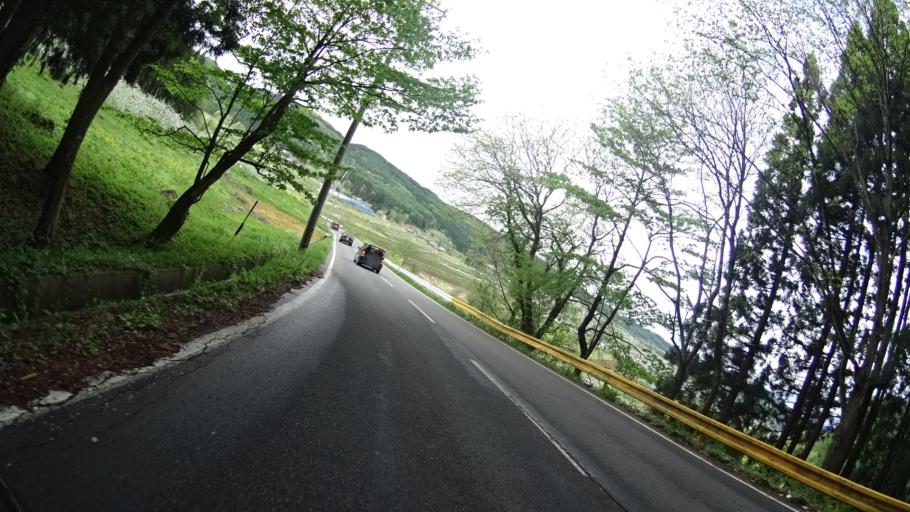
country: JP
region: Nagano
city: Nagano-shi
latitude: 36.7291
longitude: 138.2115
